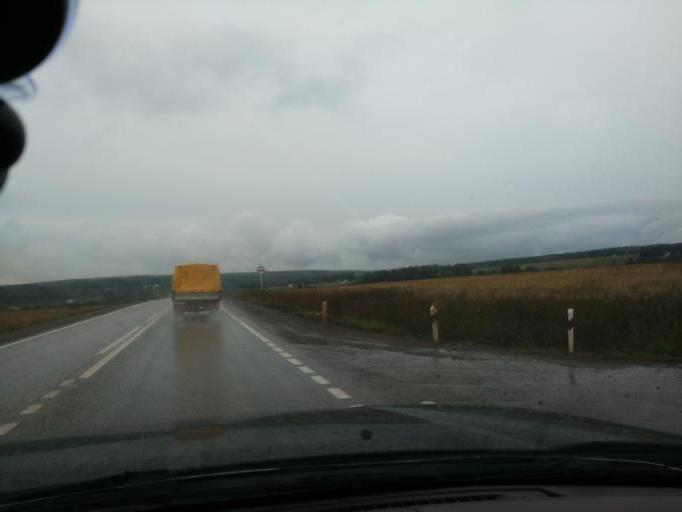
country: RU
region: Perm
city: Yugo-Kamskiy
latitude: 57.7064
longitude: 55.6300
